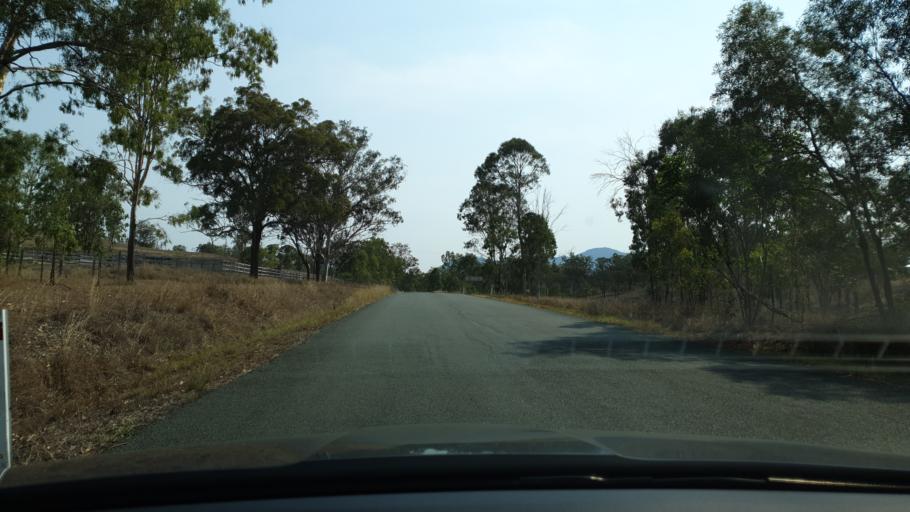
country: AU
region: Queensland
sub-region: Ipswich
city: Deebing Heights
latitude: -28.1455
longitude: 152.5653
